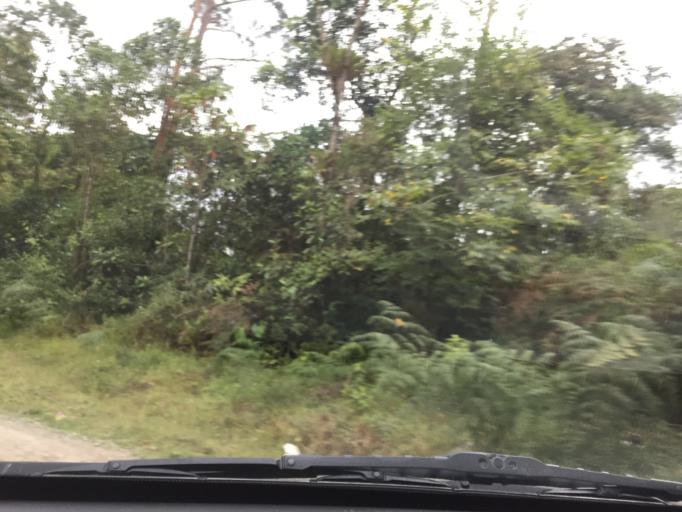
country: CO
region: Cundinamarca
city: Bojaca
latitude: 4.6789
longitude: -74.3759
